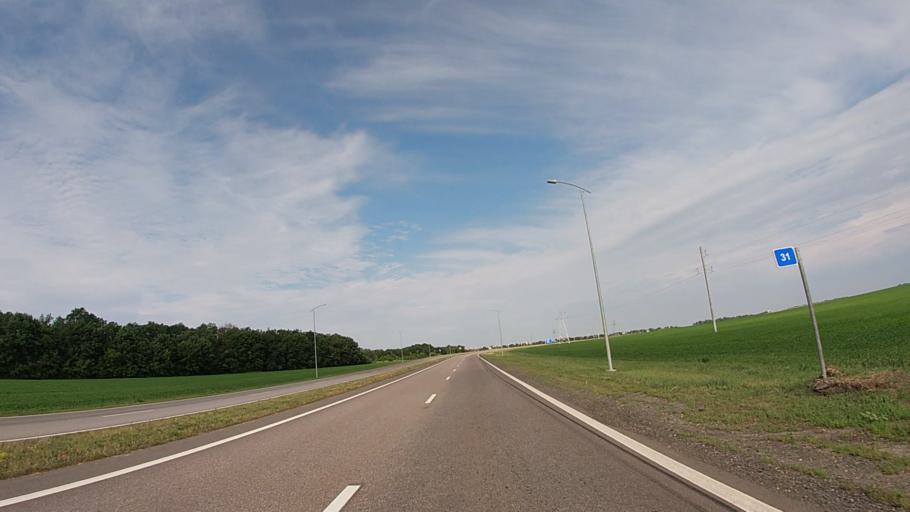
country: RU
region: Belgorod
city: Rakitnoye
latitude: 50.7903
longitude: 35.8750
